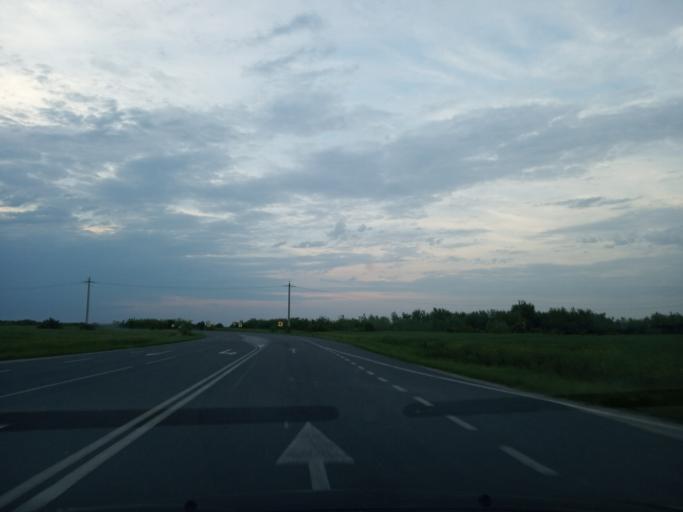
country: RO
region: Timis
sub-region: Oras Deta
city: Deta
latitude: 45.4039
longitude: 21.2383
